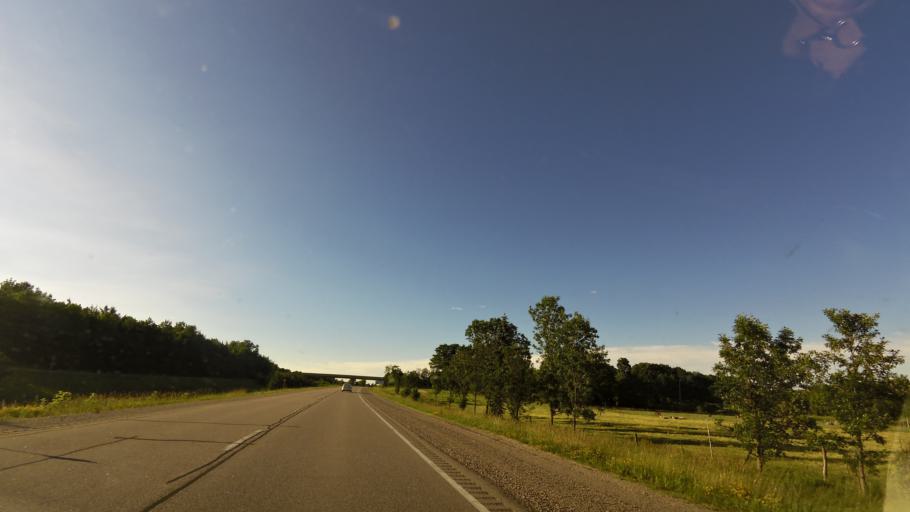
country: CA
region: Ontario
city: Orillia
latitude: 44.6818
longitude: -79.6465
